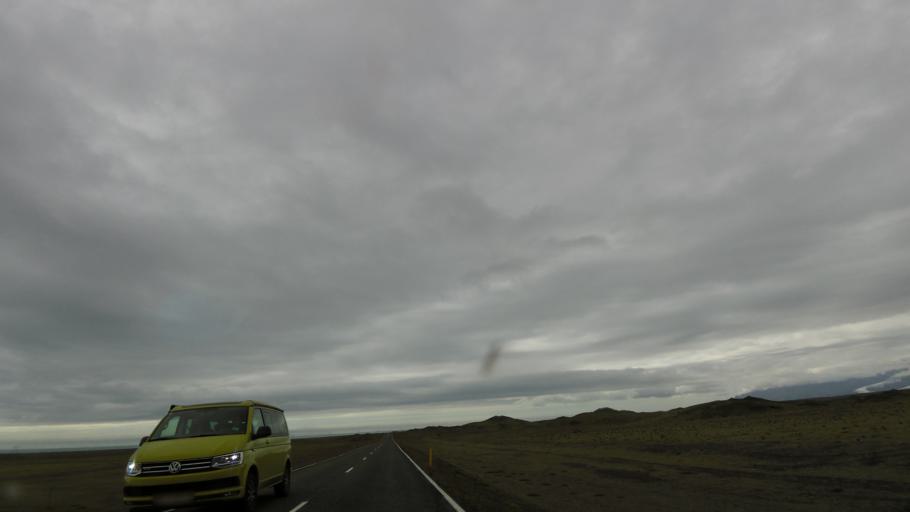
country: IS
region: East
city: Hoefn
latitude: 64.0972
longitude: -16.1004
